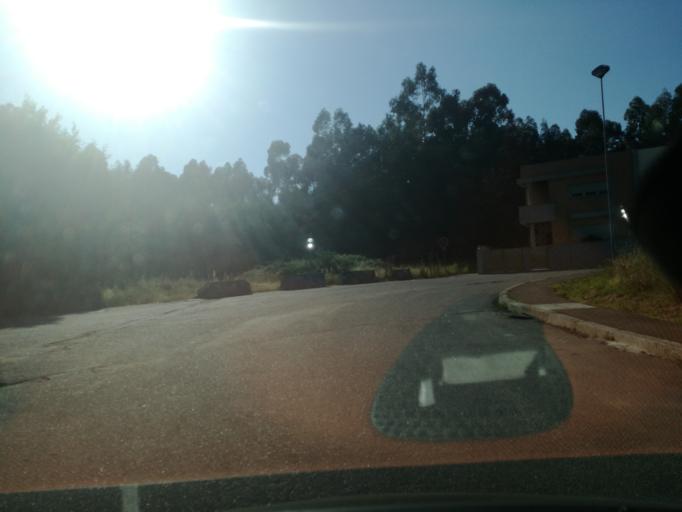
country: PT
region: Porto
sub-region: Maia
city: Gemunde
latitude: 41.2502
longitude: -8.6557
